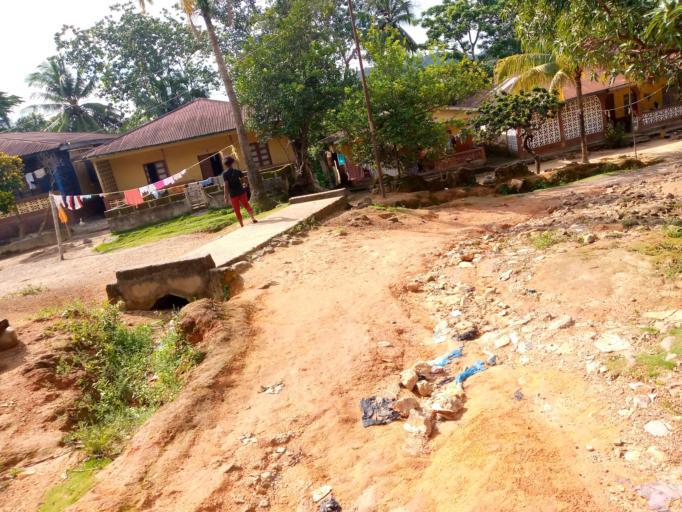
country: SL
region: Northern Province
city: Magburaka
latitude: 8.7283
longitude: -11.9473
